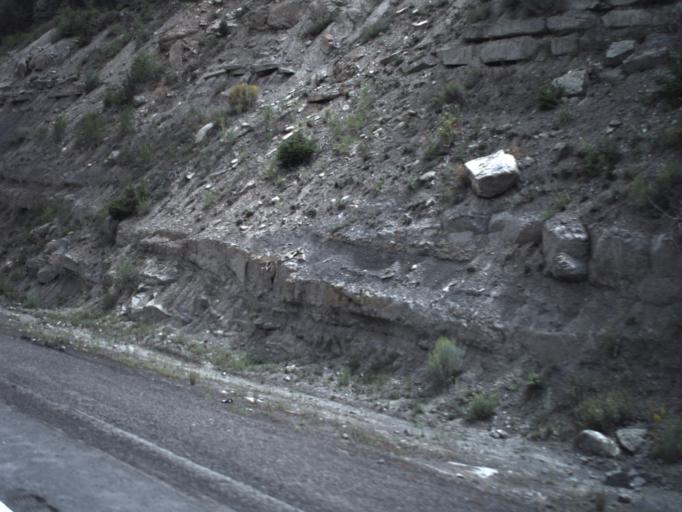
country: US
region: Utah
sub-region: Carbon County
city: Helper
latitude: 39.8022
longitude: -110.9390
